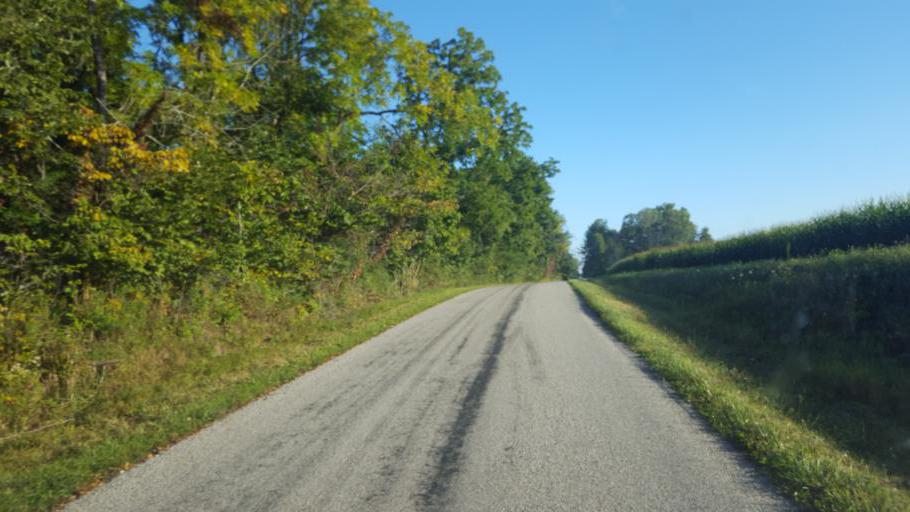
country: US
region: Ohio
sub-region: Lorain County
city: Wellington
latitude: 41.1053
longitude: -82.2788
